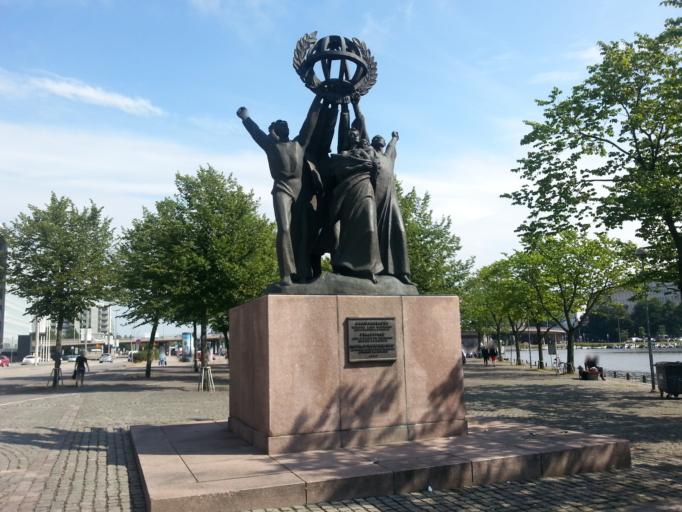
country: FI
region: Uusimaa
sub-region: Helsinki
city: Helsinki
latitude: 60.1782
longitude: 24.9534
